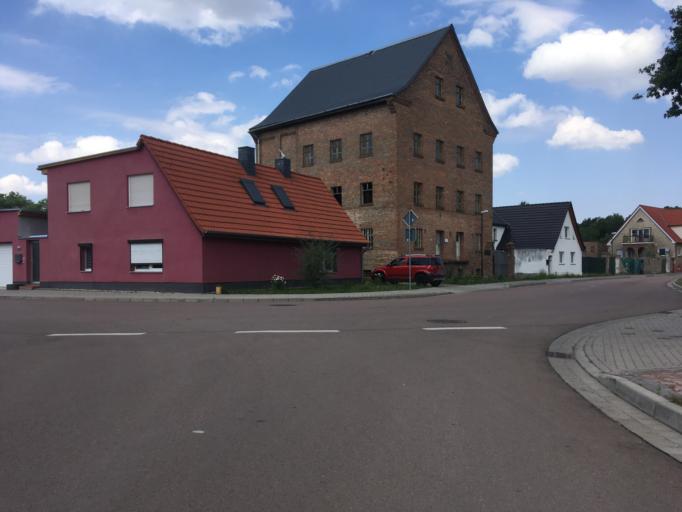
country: DE
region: Saxony-Anhalt
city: Quellendorf
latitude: 51.7689
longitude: 12.0762
